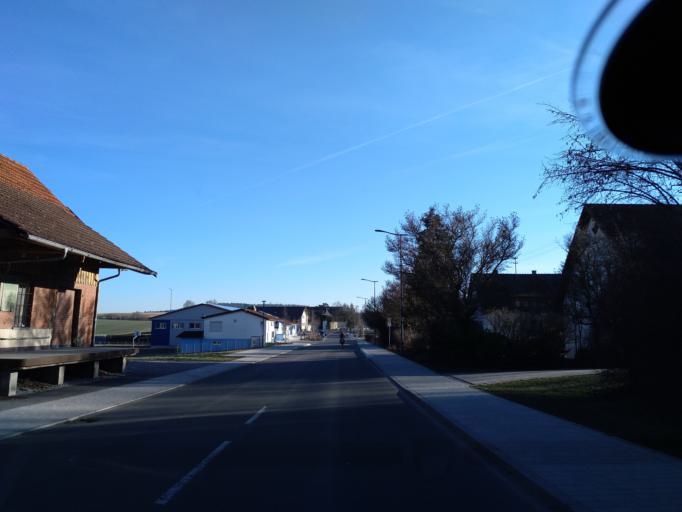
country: DE
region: Baden-Wuerttemberg
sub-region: Regierungsbezirk Stuttgart
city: Rosenberg
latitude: 49.0811
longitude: 9.9787
